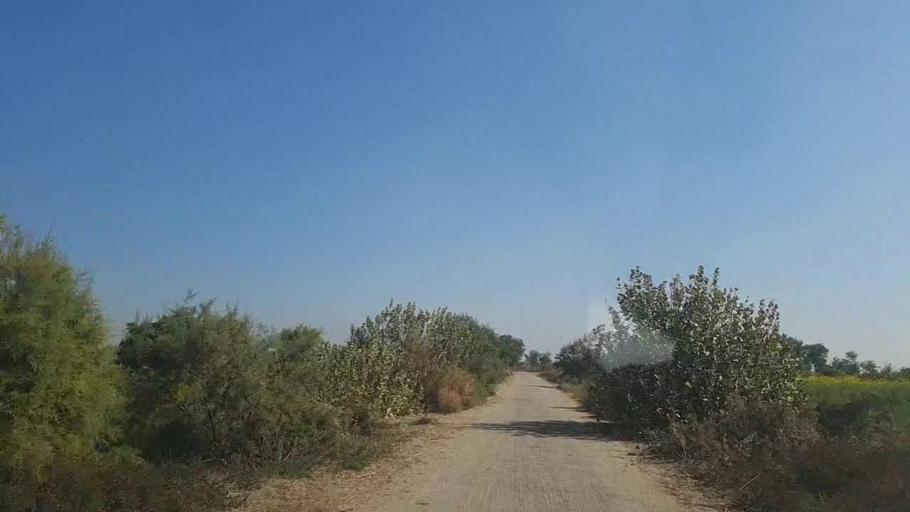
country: PK
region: Sindh
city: Sinjhoro
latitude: 26.1588
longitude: 68.8586
